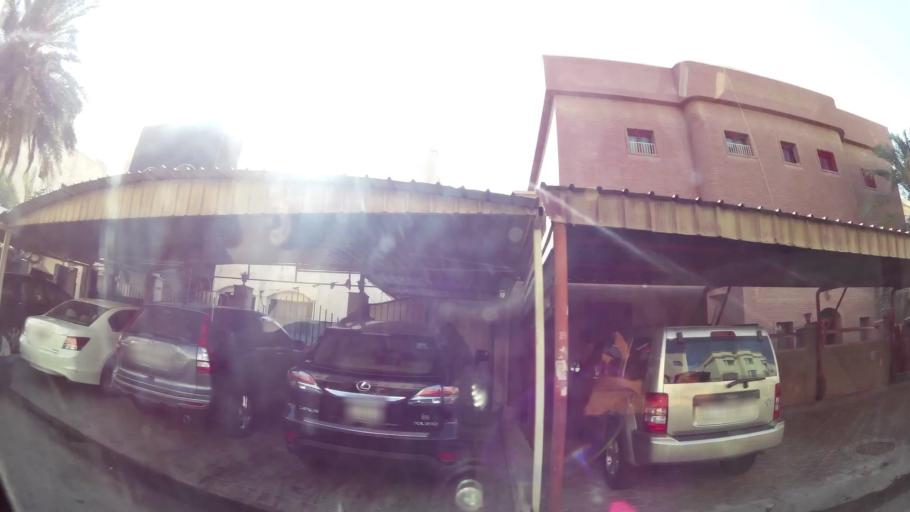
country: KW
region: Muhafazat Hawalli
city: Salwa
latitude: 29.2908
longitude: 48.0774
